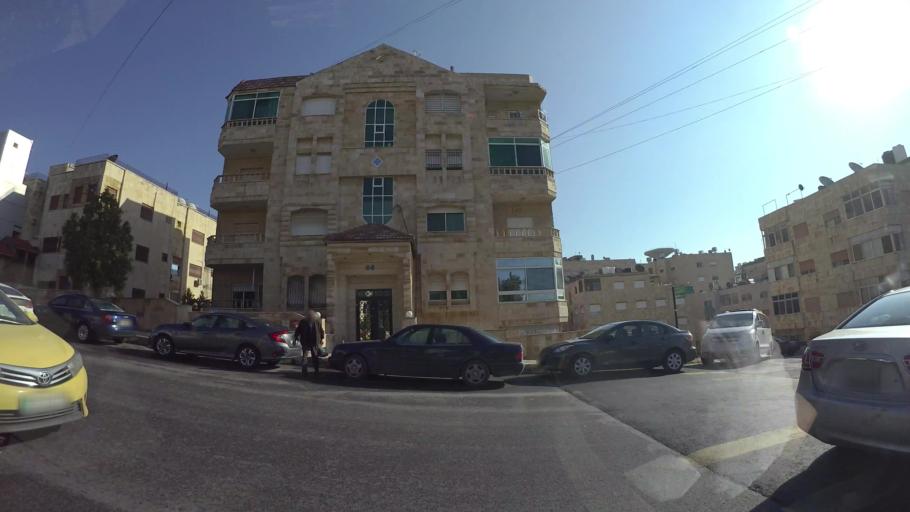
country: JO
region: Amman
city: Al Jubayhah
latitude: 31.9992
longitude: 35.8864
